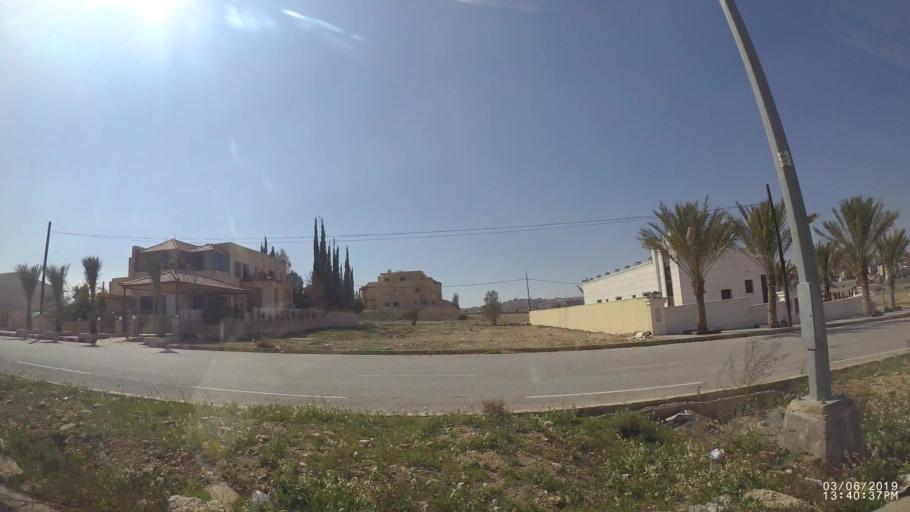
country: JO
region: Zarqa
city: Zarqa
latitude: 32.0741
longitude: 36.1074
